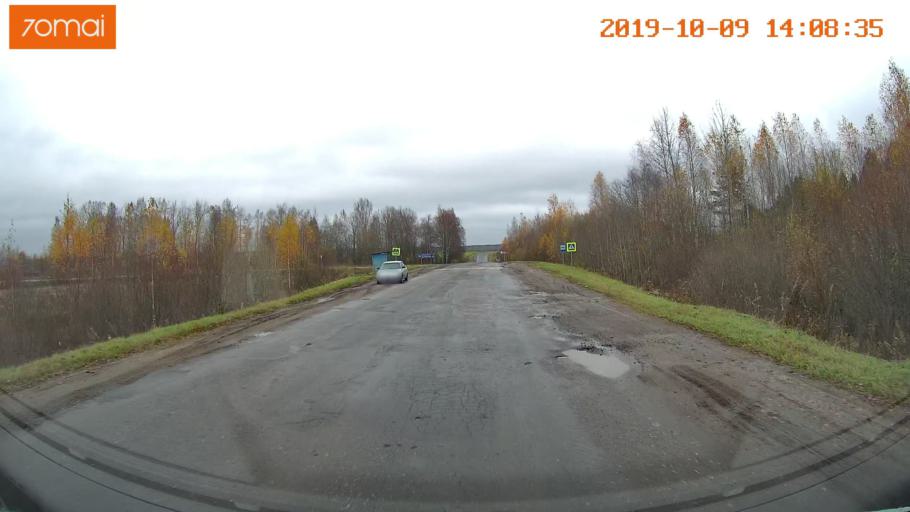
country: RU
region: Kostroma
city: Buy
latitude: 58.4776
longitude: 41.4379
